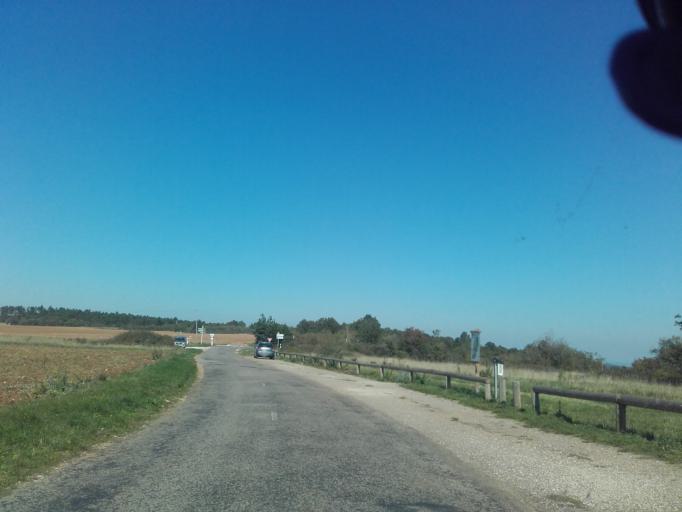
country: FR
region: Bourgogne
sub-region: Departement de la Cote-d'Or
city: Meursault
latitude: 47.0028
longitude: 4.7006
